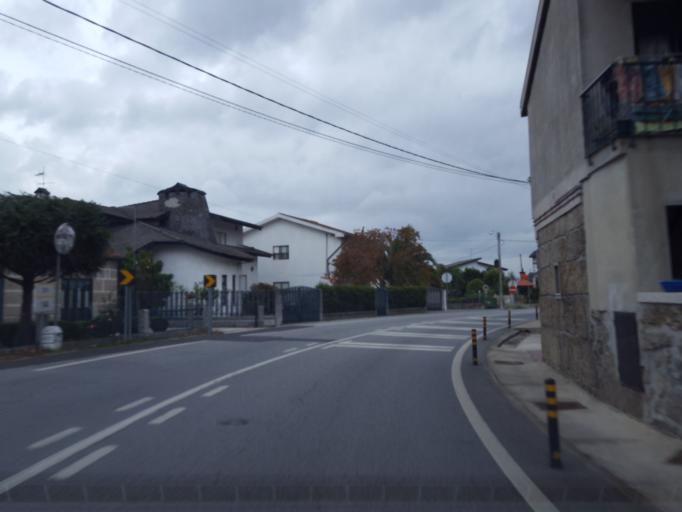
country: PT
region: Porto
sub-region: Marco de Canaveses
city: Marco de Canavezes
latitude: 41.1694
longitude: -8.1508
